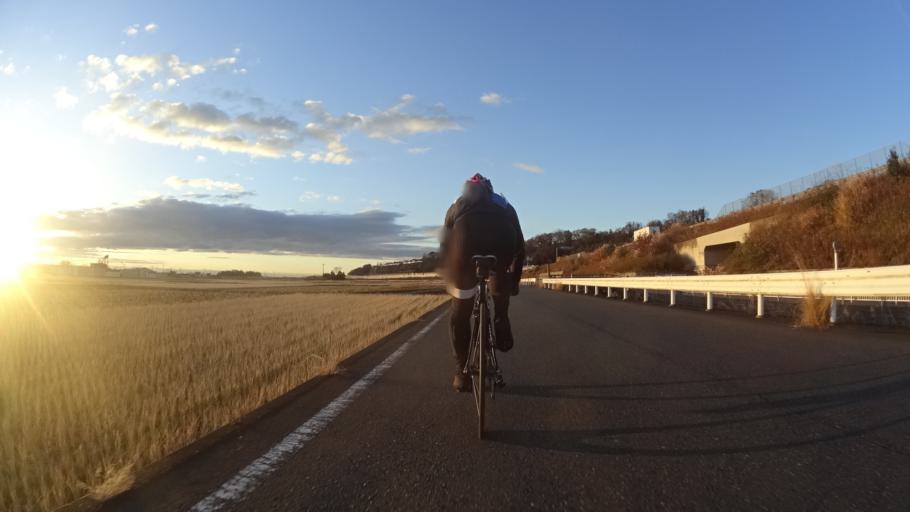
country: JP
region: Kanagawa
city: Zama
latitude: 35.5050
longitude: 139.3667
